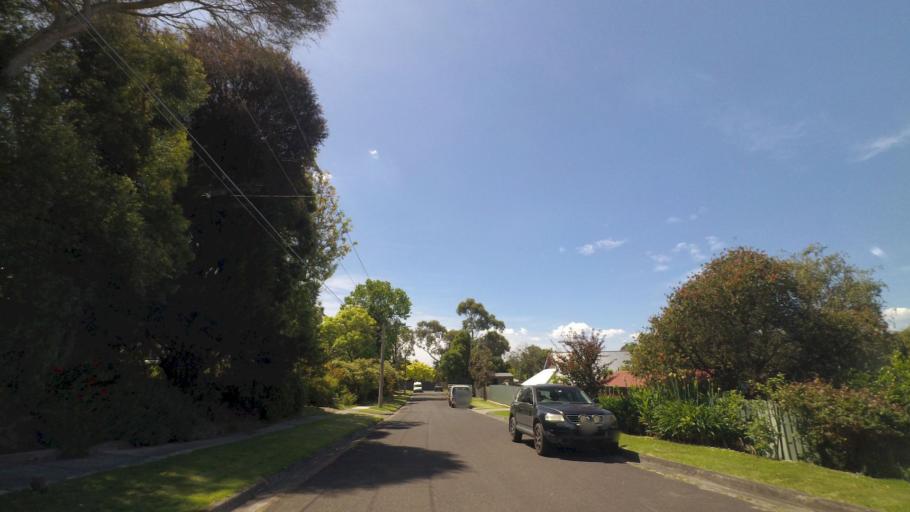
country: AU
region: Victoria
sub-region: Yarra Ranges
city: Montrose
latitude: -37.8069
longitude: 145.3461
